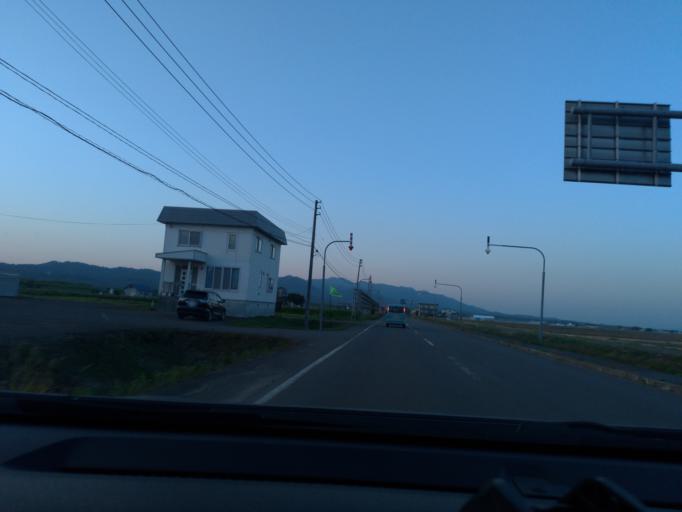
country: JP
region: Hokkaido
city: Iwamizawa
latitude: 43.3291
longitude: 141.7030
